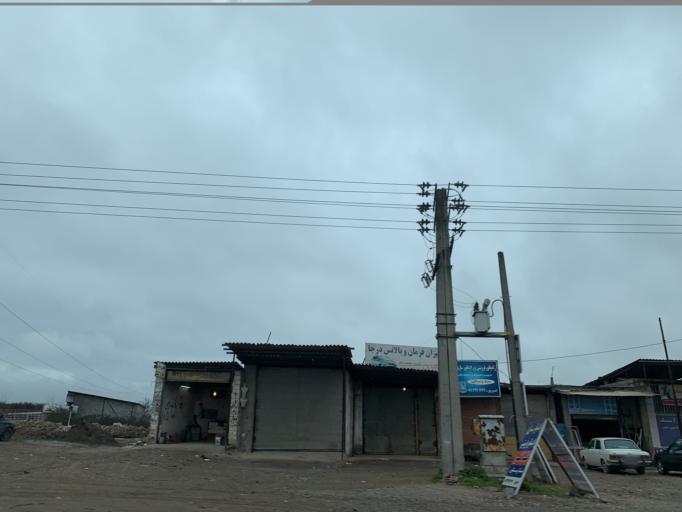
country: IR
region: Mazandaran
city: Amol
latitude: 36.4146
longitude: 52.3483
